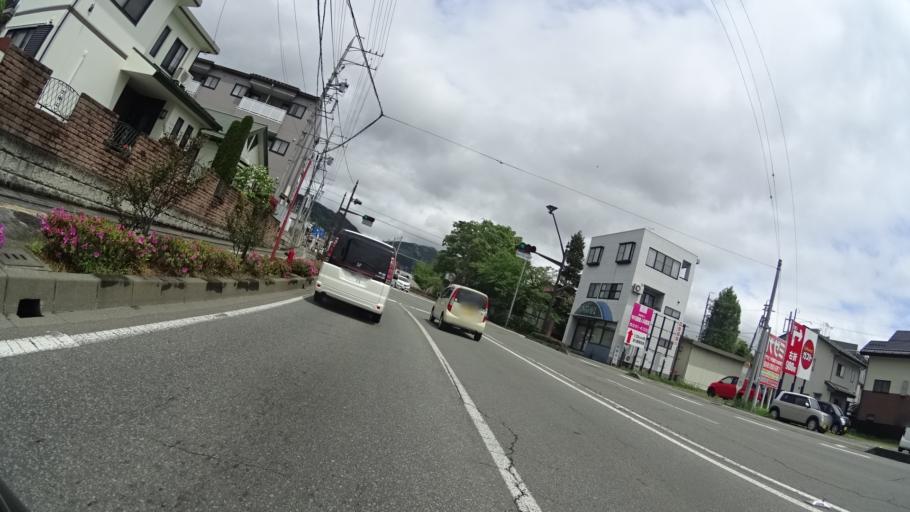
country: JP
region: Nagano
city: Nagano-shi
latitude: 36.6685
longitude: 138.1979
